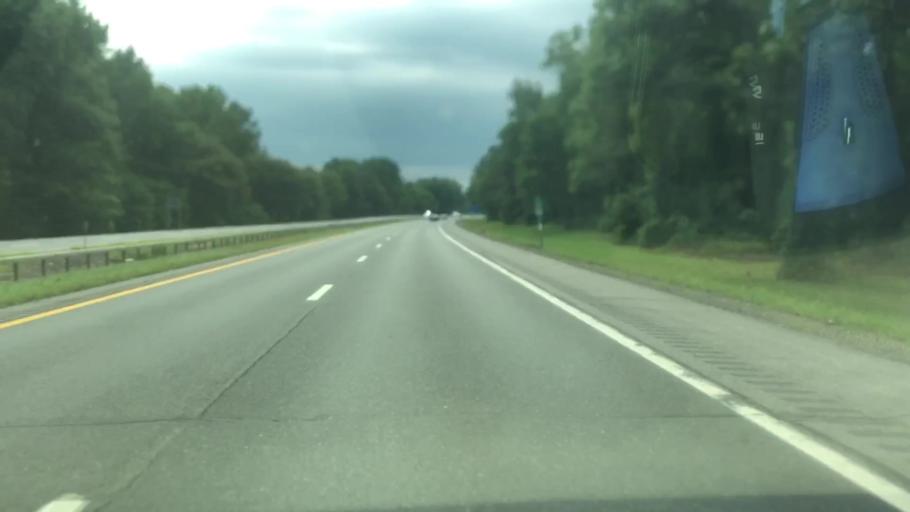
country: US
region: New York
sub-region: Schenectady County
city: Rotterdam
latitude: 42.7652
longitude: -73.9285
